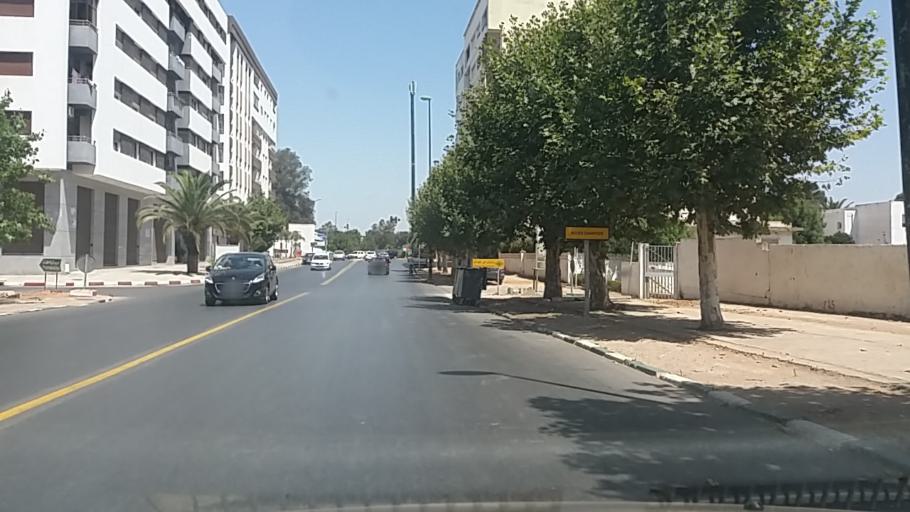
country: MA
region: Gharb-Chrarda-Beni Hssen
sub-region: Kenitra Province
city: Kenitra
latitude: 34.2551
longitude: -6.5765
